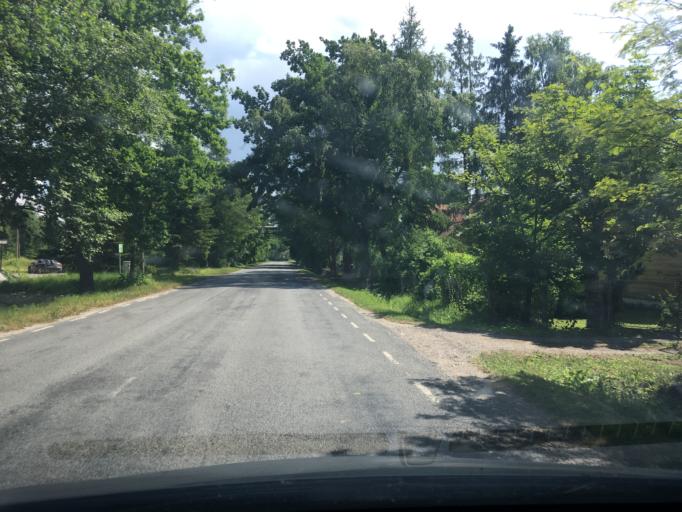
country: EE
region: Paernumaa
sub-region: Halinga vald
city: Parnu-Jaagupi
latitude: 58.7154
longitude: 24.3618
